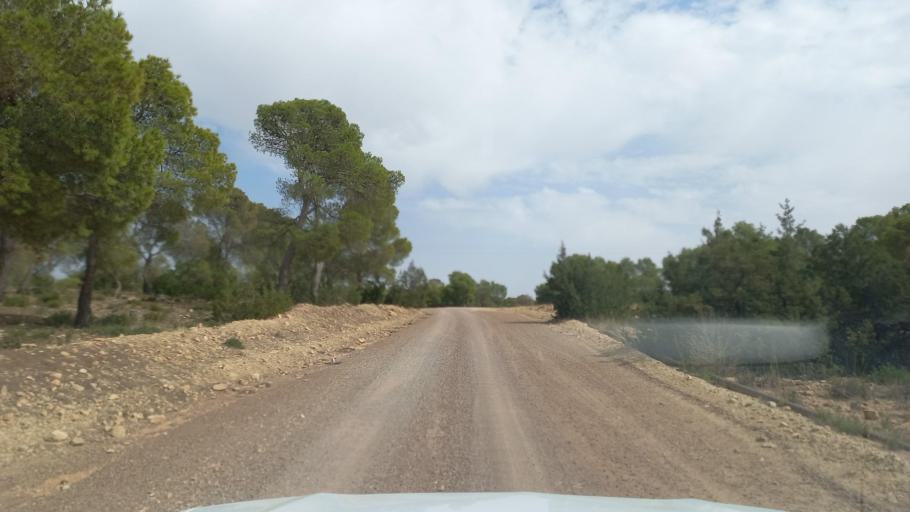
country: TN
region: Al Qasrayn
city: Kasserine
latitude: 35.3820
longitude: 8.8912
